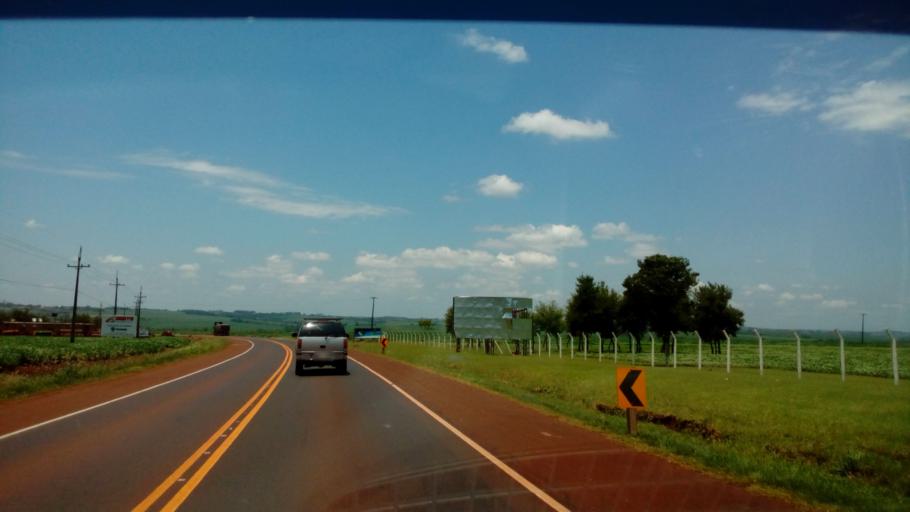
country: PY
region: Alto Parana
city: Naranjal
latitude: -25.8864
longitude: -55.1229
